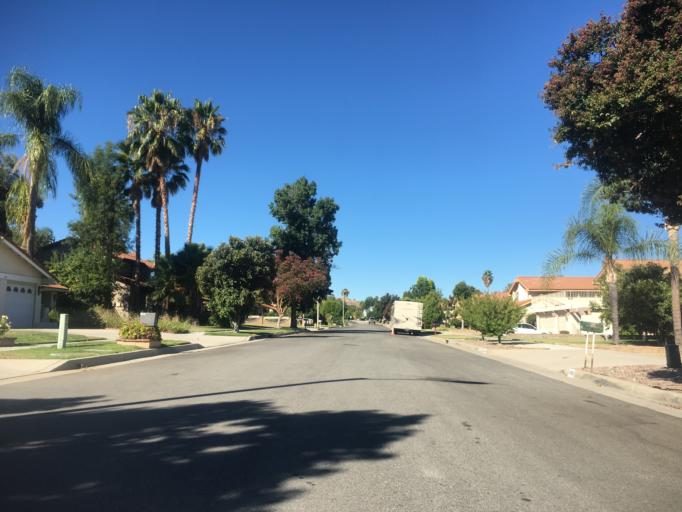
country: US
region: California
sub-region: San Bernardino County
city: Redlands
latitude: 34.0439
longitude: -117.2020
